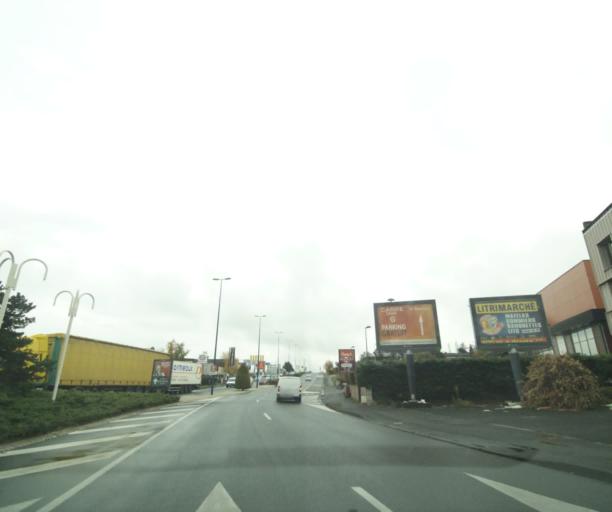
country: FR
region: Auvergne
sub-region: Departement du Puy-de-Dome
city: Aubiere
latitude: 45.7641
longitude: 3.1256
